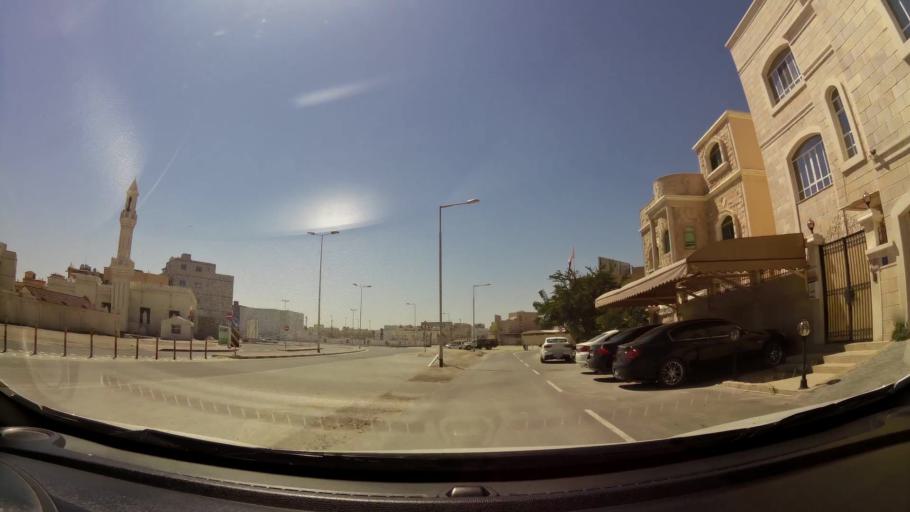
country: BH
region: Muharraq
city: Al Muharraq
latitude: 26.2730
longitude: 50.6028
